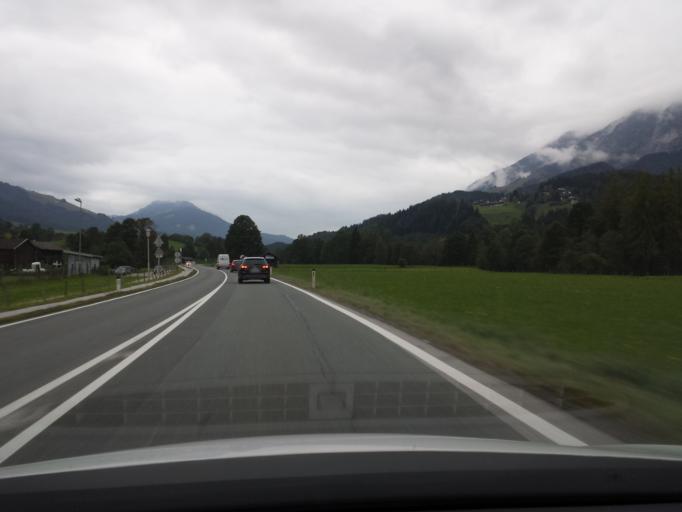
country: AT
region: Salzburg
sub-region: Politischer Bezirk Zell am See
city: Leogang
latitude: 47.4392
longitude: 12.7780
